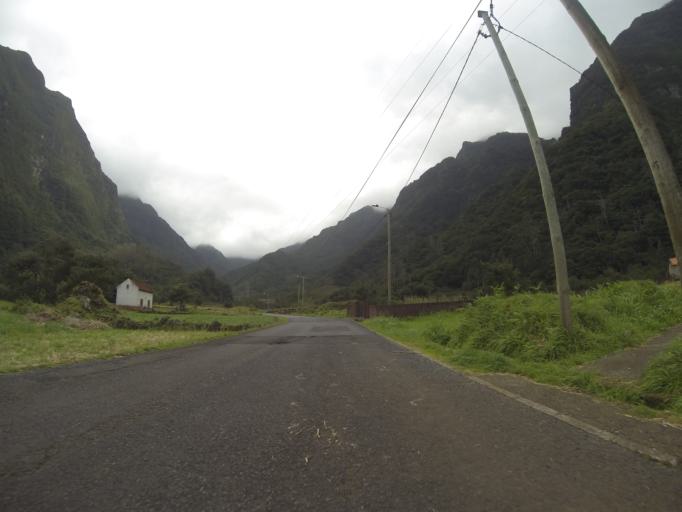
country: PT
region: Madeira
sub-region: Porto Moniz
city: Porto Moniz
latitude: 32.8055
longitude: -17.1154
